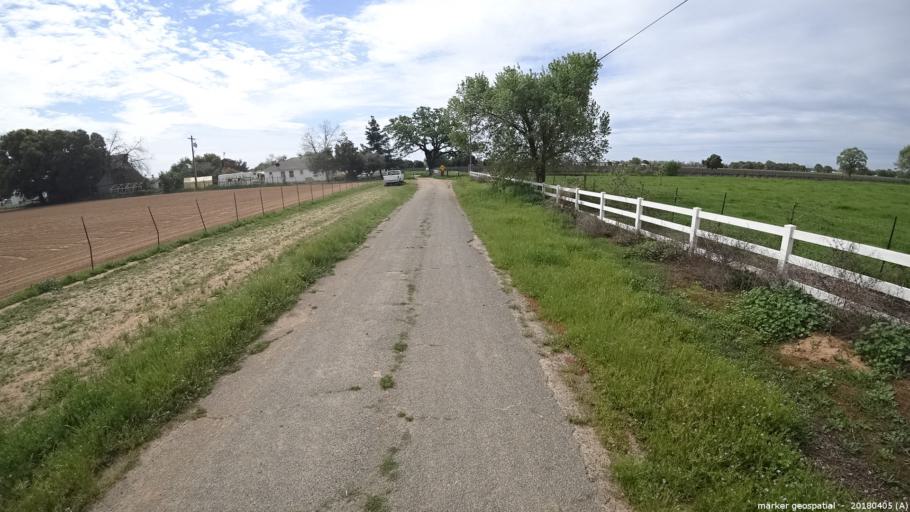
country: US
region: California
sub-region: Sacramento County
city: Galt
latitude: 38.2448
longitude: -121.3374
